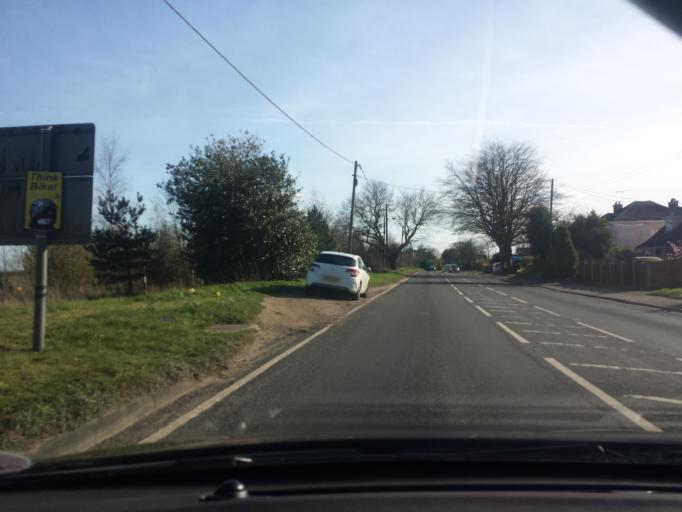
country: GB
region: England
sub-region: Essex
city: Alresford
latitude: 51.8407
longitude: 1.0285
